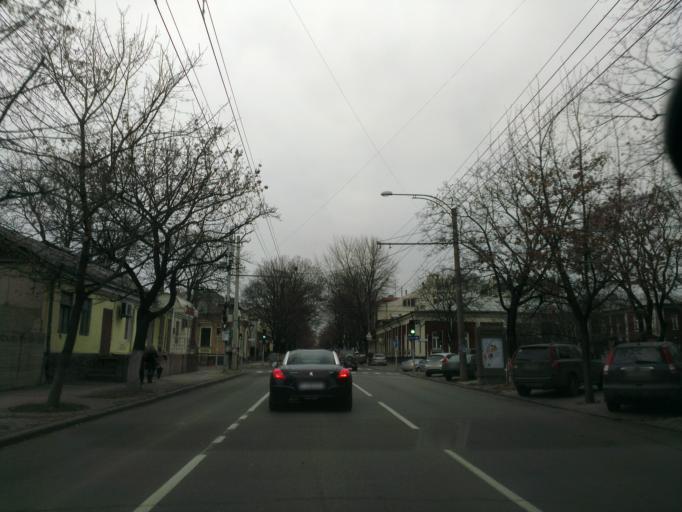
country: MD
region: Chisinau
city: Chisinau
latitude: 47.0184
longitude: 28.8329
